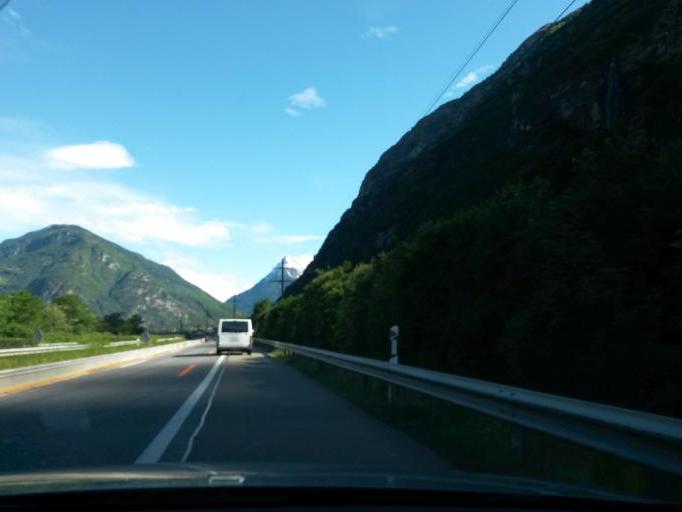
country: CH
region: Ticino
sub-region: Riviera District
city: Lodrino
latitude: 46.3214
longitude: 8.9809
